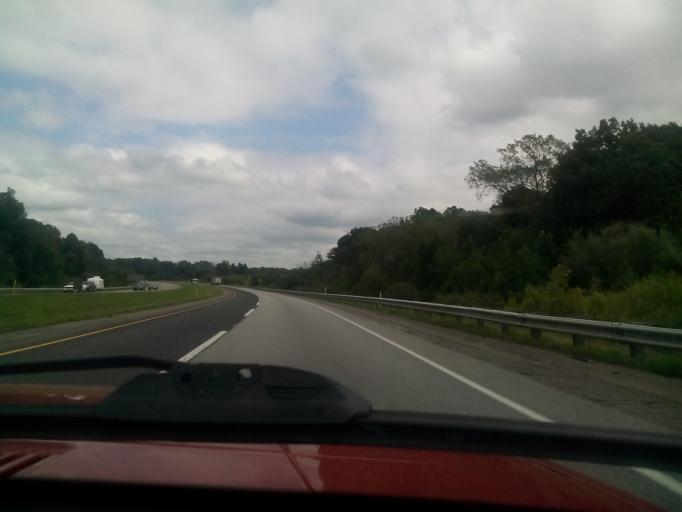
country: US
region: Indiana
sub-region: LaPorte County
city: Westville
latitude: 41.5944
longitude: -86.8739
